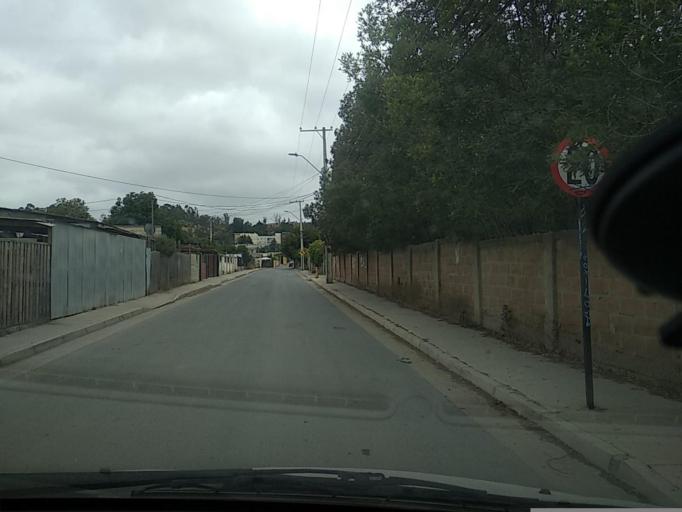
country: CL
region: Valparaiso
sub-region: Provincia de Marga Marga
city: Villa Alemana
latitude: -33.0381
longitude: -71.3586
